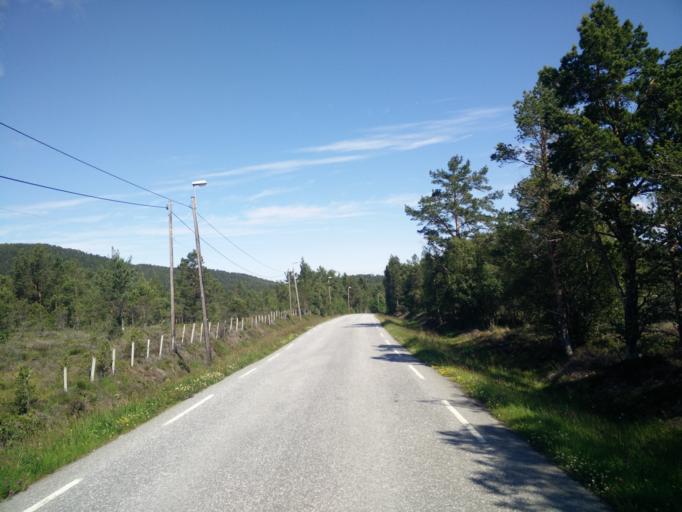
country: NO
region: More og Romsdal
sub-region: Kristiansund
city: Rensvik
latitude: 63.0643
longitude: 7.8689
